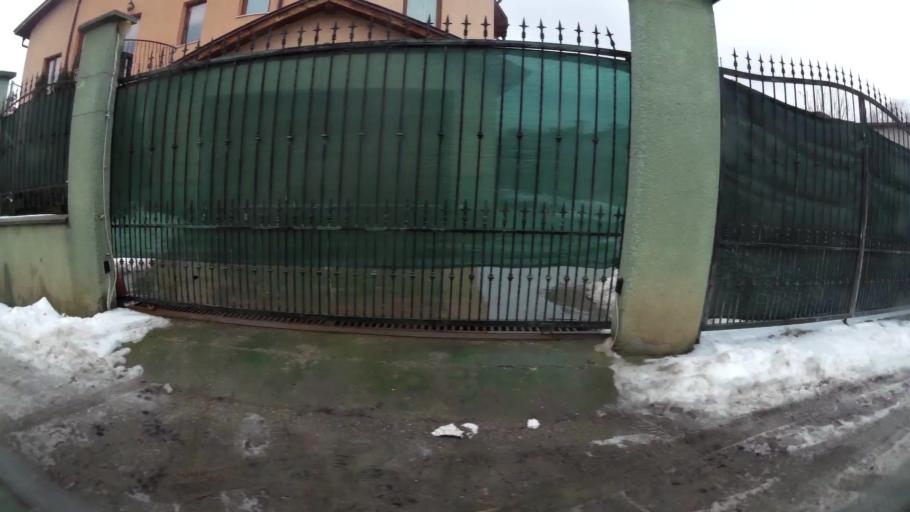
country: BG
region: Sofia-Capital
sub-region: Stolichna Obshtina
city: Sofia
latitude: 42.6505
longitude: 23.2974
